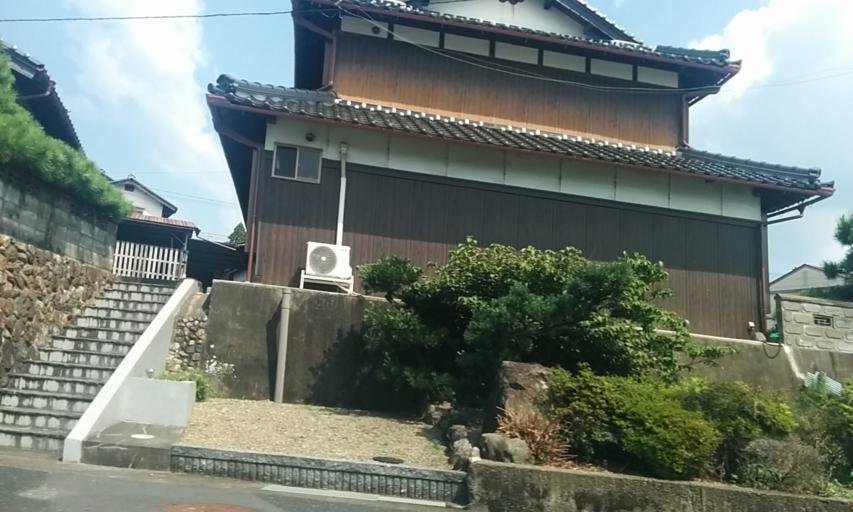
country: JP
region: Kyoto
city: Fukuchiyama
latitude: 35.3103
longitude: 135.1294
